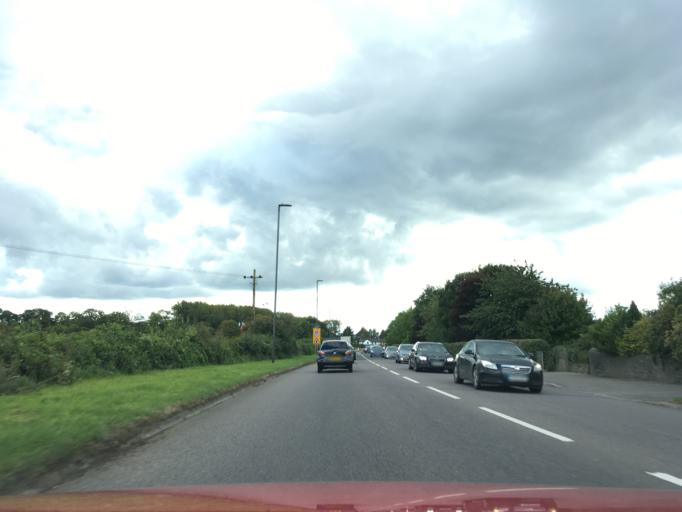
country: GB
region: England
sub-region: South Gloucestershire
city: Alveston
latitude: 51.5873
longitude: -2.5280
